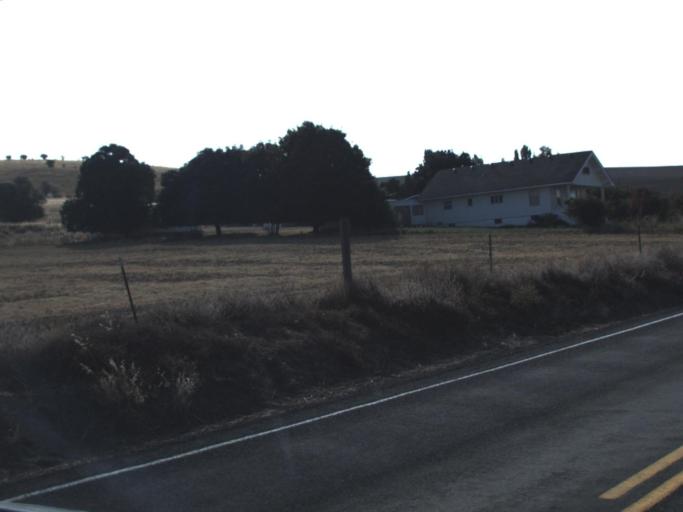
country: US
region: Idaho
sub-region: Benewah County
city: Plummer
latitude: 47.2564
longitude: -117.1301
